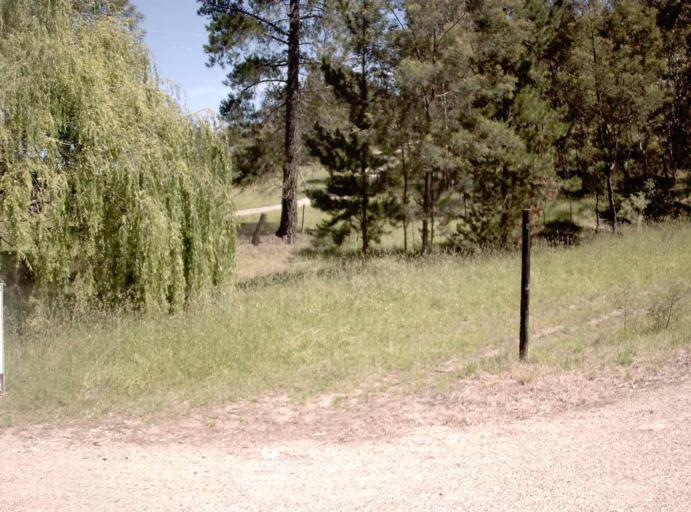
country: AU
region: Victoria
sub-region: East Gippsland
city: Lakes Entrance
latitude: -37.3405
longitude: 148.2284
